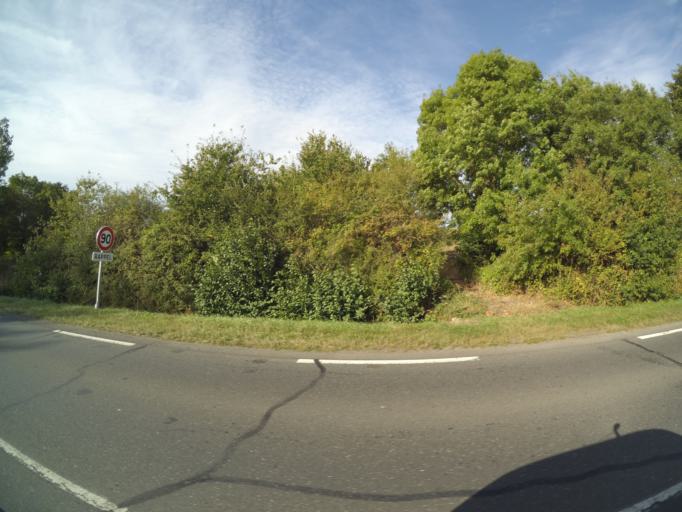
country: FR
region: Pays de la Loire
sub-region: Departement de la Loire-Atlantique
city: Mouzillon
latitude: 47.1166
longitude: -1.2827
